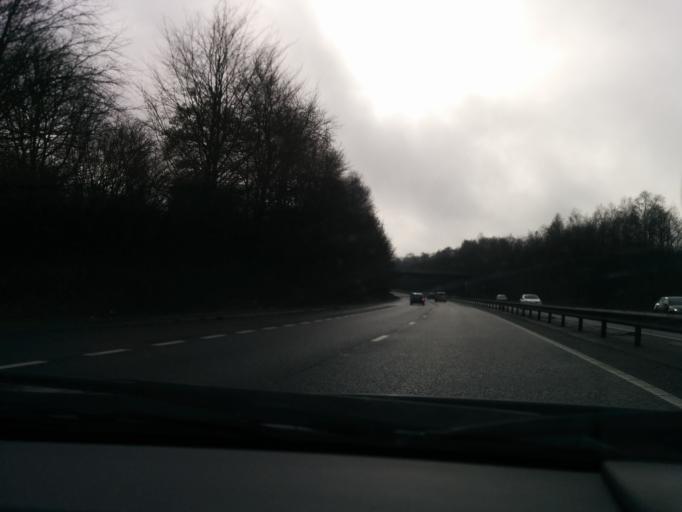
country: GB
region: England
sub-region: Hampshire
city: Highclere
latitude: 51.2764
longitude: -1.3439
